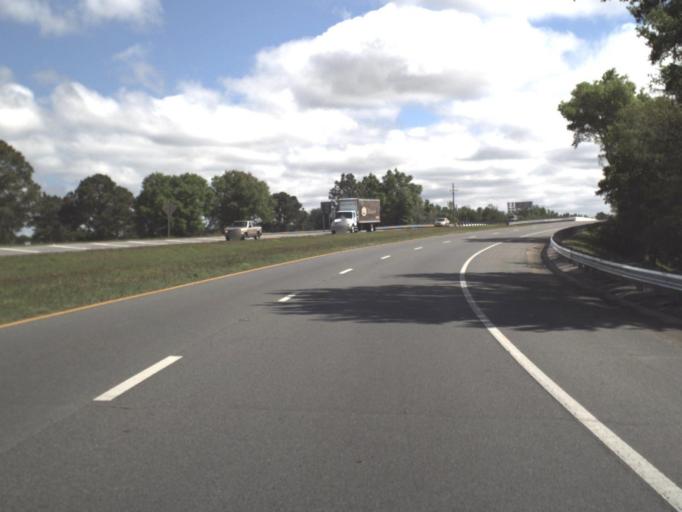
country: US
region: Florida
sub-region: Escambia County
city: West Pensacola
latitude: 30.4291
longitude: -87.2742
